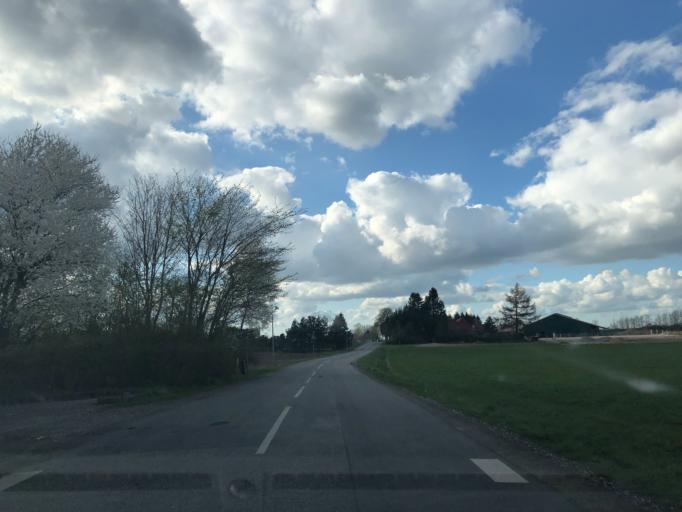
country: DK
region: Zealand
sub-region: Lejre Kommune
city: Kirke Hvalso
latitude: 55.5099
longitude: 11.8800
